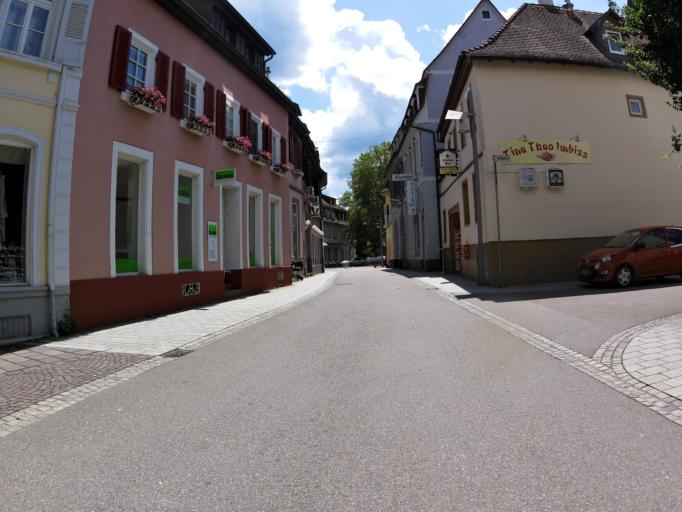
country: DE
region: Baden-Wuerttemberg
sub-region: Freiburg Region
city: Lahr
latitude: 48.3399
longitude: 7.8736
